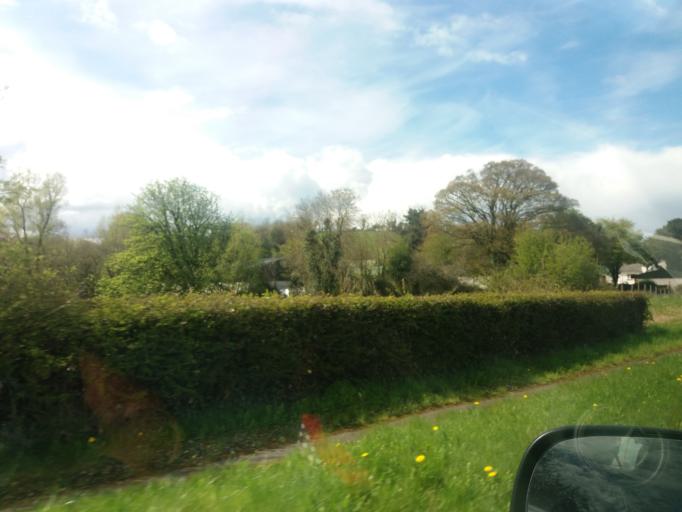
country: GB
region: Northern Ireland
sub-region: Fermanagh District
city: Enniskillen
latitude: 54.3670
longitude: -7.6798
